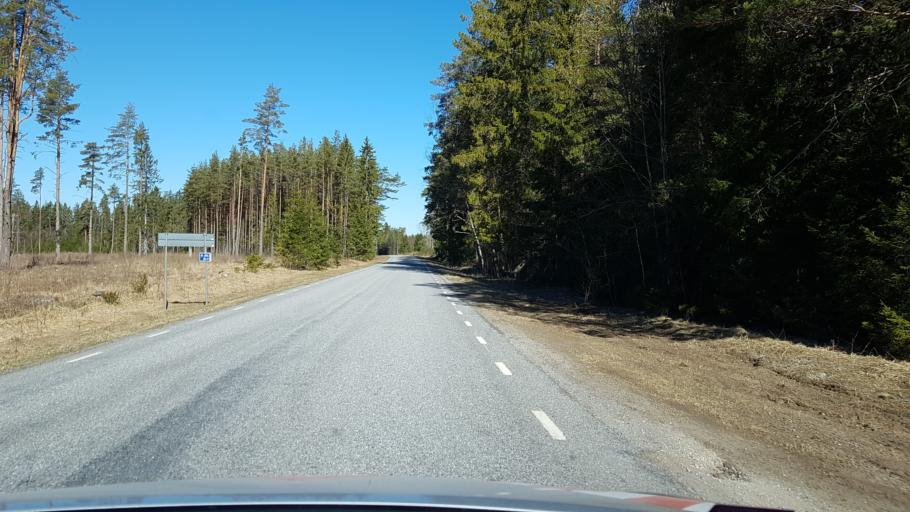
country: EE
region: Laeaene-Virumaa
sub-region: Haljala vald
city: Haljala
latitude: 59.4940
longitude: 26.2441
